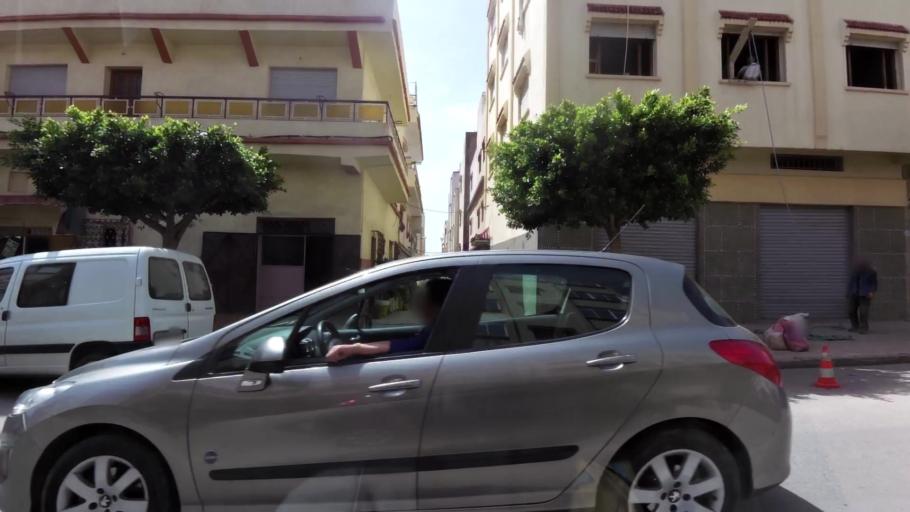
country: MA
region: Tanger-Tetouan
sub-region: Tanger-Assilah
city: Tangier
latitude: 35.7584
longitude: -5.8378
